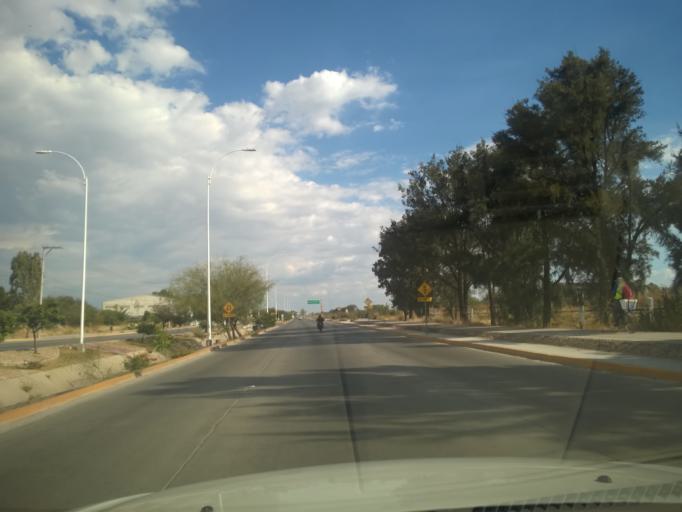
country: MX
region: Guanajuato
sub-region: Leon
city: San Jose de Duran (Los Troncoso)
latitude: 21.0750
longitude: -101.6500
